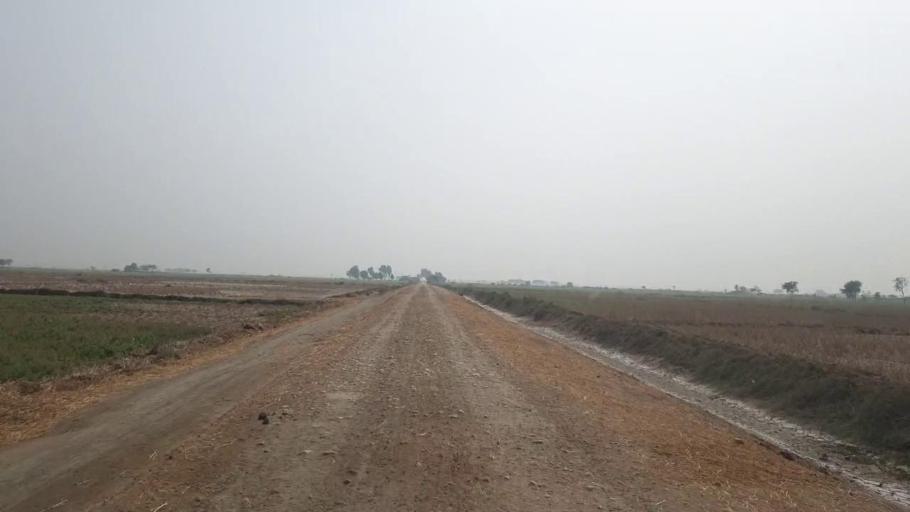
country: PK
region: Sindh
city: Kario
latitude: 24.6369
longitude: 68.5958
